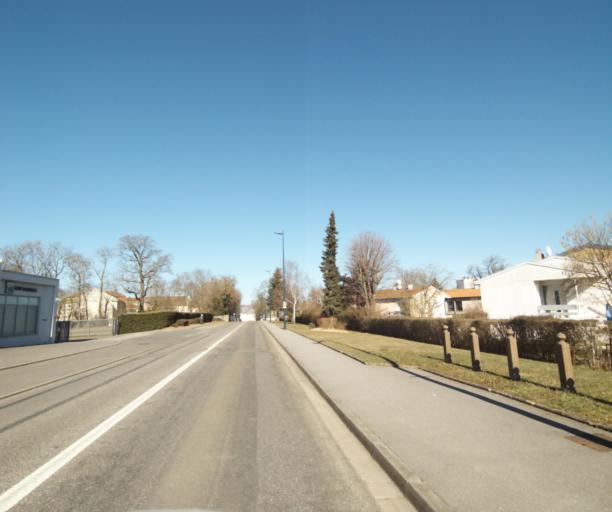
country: FR
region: Lorraine
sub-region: Departement de Meurthe-et-Moselle
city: Jarville-la-Malgrange
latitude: 48.6640
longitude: 6.2078
